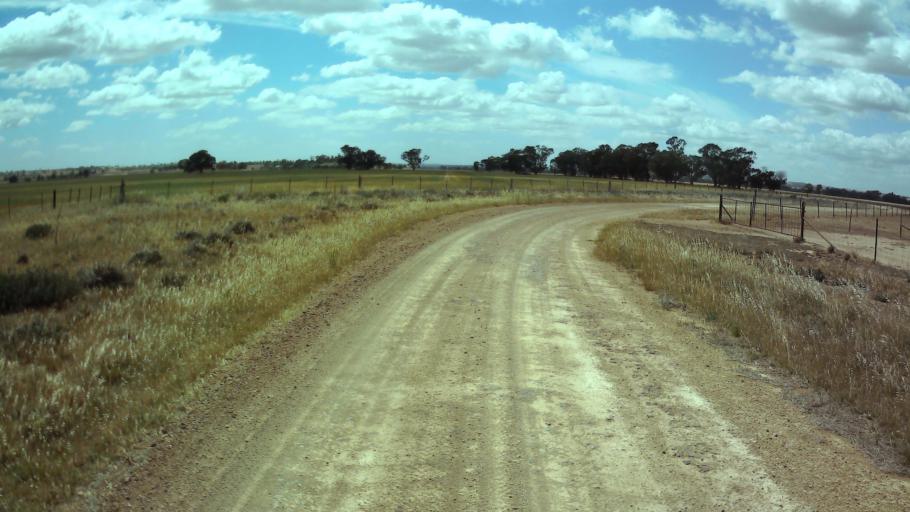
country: AU
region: New South Wales
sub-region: Weddin
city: Grenfell
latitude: -33.9967
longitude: 148.2926
